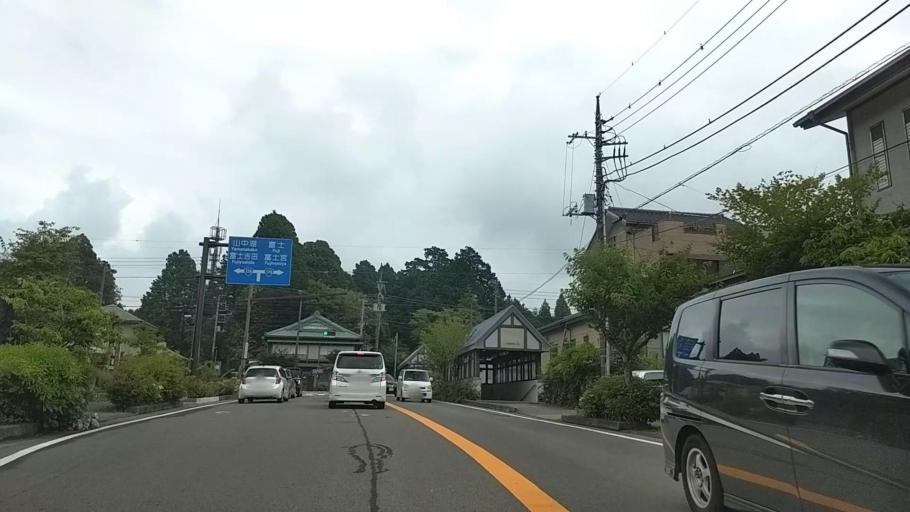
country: JP
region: Yamanashi
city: Fujikawaguchiko
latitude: 35.4628
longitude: 138.6050
